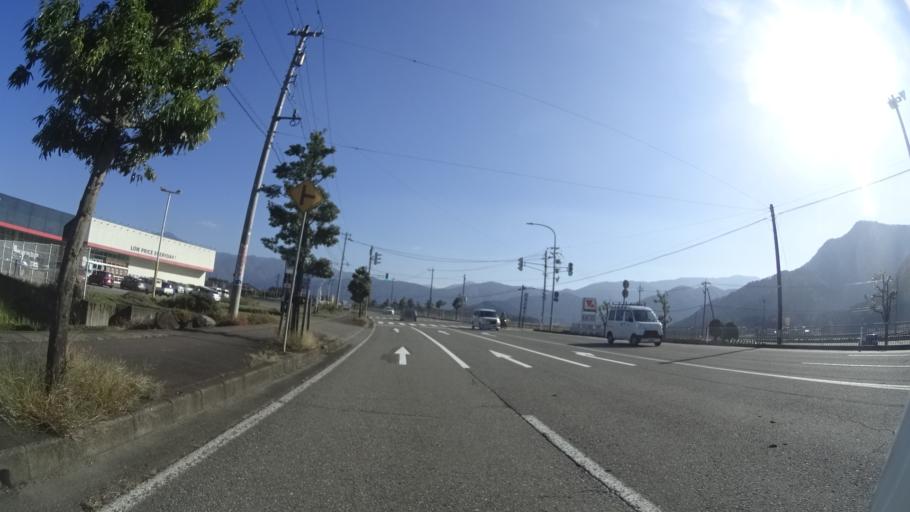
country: JP
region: Fukui
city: Ono
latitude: 35.9734
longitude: 136.4809
